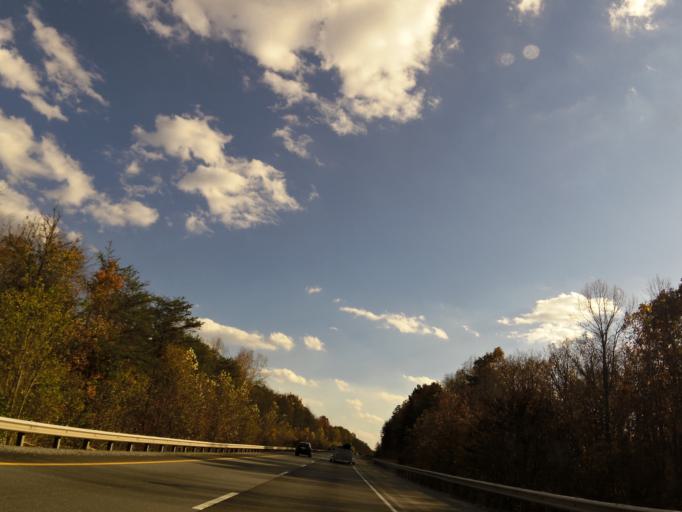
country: US
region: Tennessee
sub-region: Campbell County
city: Jacksboro
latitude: 36.3634
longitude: -84.2334
